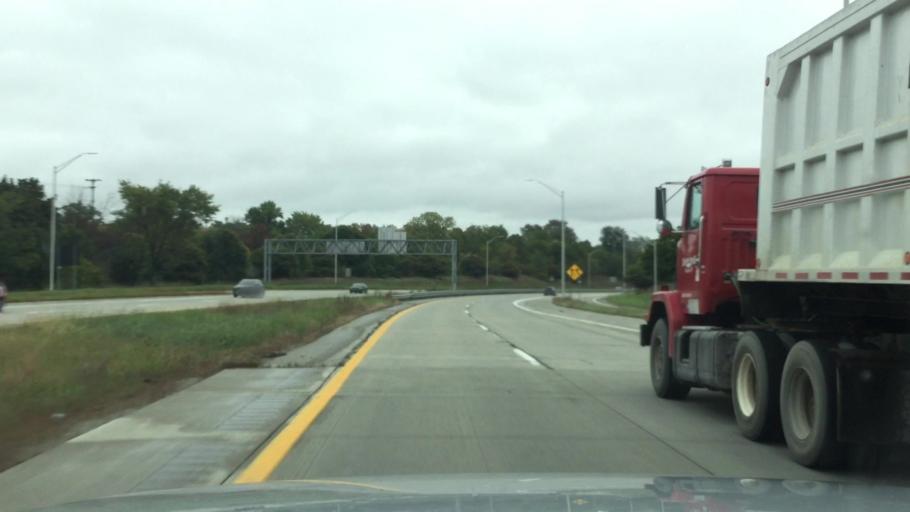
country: US
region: Michigan
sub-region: Saginaw County
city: Carrollton
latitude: 43.4359
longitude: -83.9248
